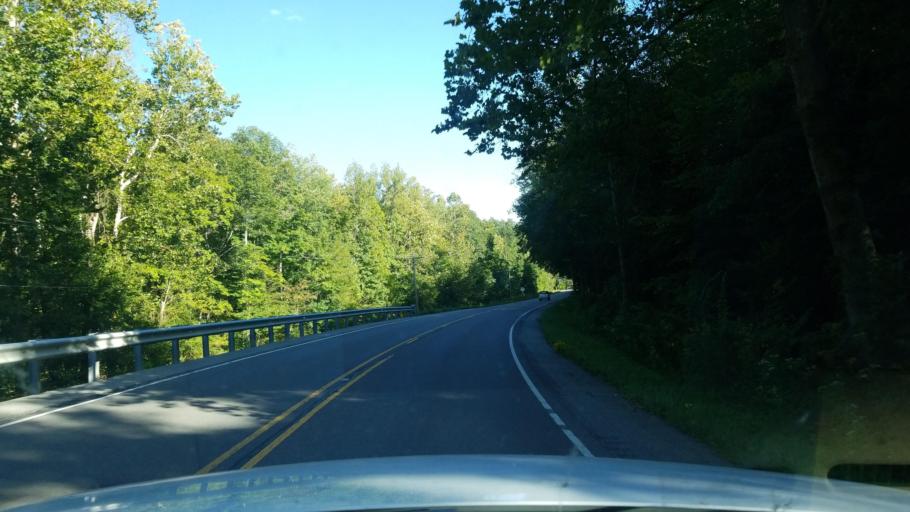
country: US
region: Illinois
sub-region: Saline County
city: Harrisburg
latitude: 37.5872
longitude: -88.4458
